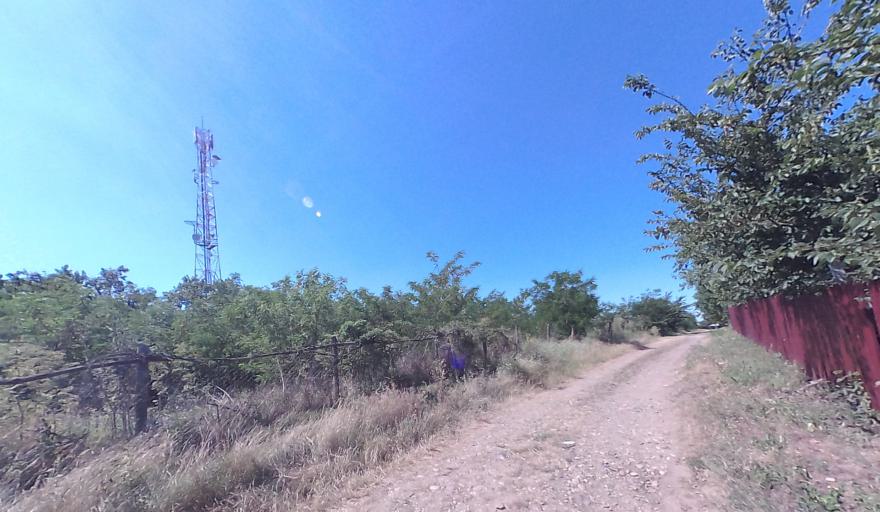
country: RO
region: Vaslui
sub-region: Comuna Costesti
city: Costesti
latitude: 46.4800
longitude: 27.7929
